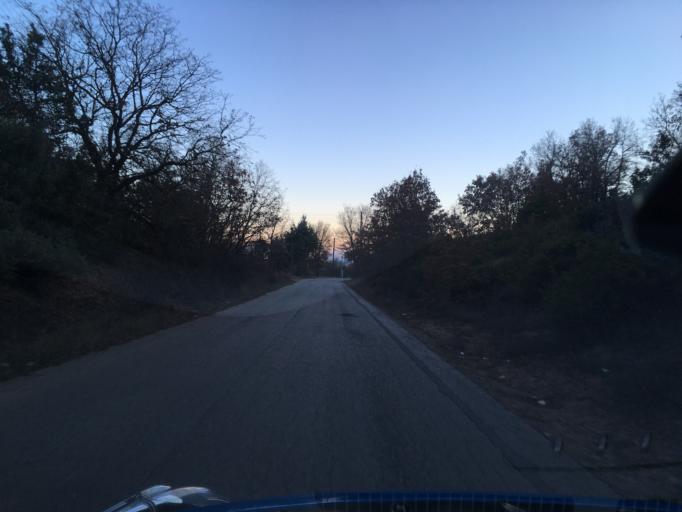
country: GR
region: West Macedonia
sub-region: Nomos Kozanis
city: Kozani
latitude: 40.2609
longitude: 21.7498
